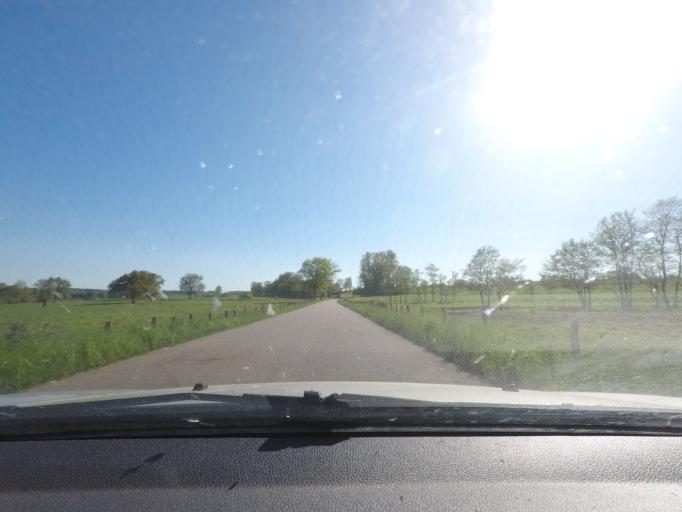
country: BE
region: Wallonia
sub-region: Province du Luxembourg
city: Tintigny
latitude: 49.7136
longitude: 5.4803
